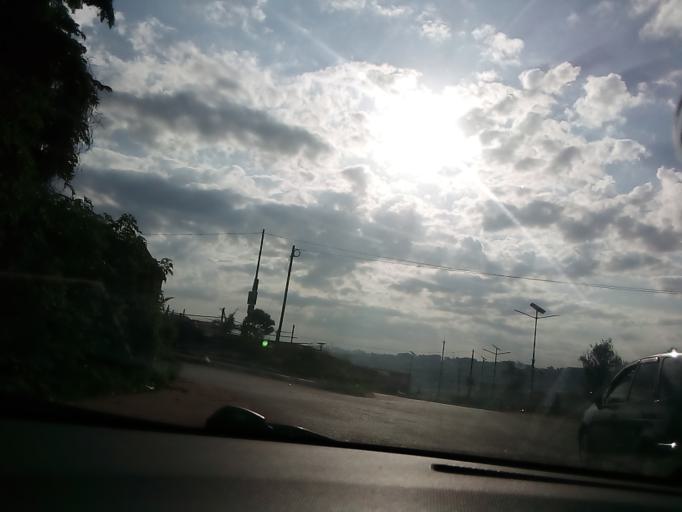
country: UG
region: Central Region
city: Masaka
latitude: -0.3483
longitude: 31.7380
